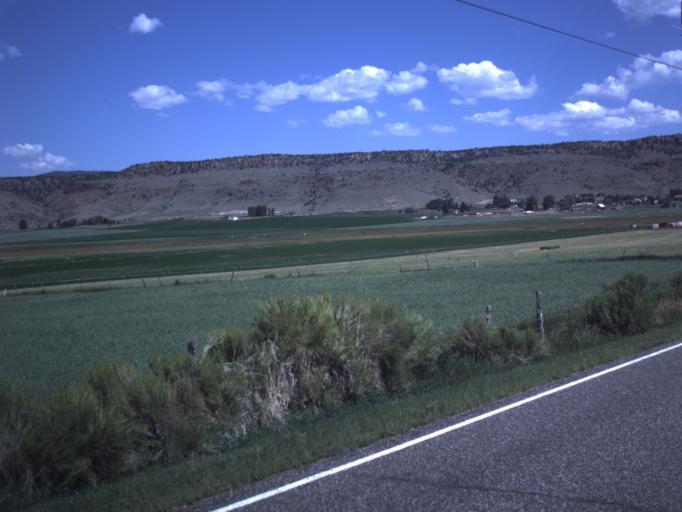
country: US
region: Utah
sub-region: Wayne County
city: Loa
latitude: 38.4418
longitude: -111.6158
